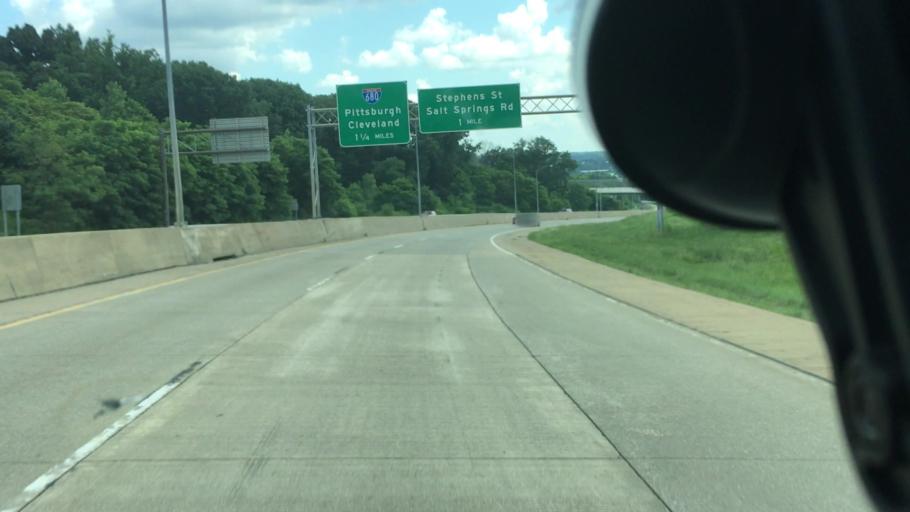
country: US
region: Ohio
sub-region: Trumbull County
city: Churchill
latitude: 41.1280
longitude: -80.6740
